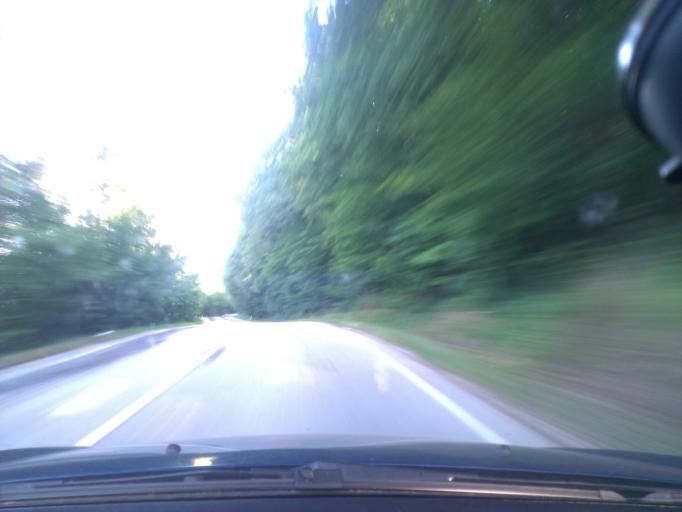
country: SK
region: Trenciansky
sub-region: Okres Myjava
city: Myjava
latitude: 48.8084
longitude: 17.5258
